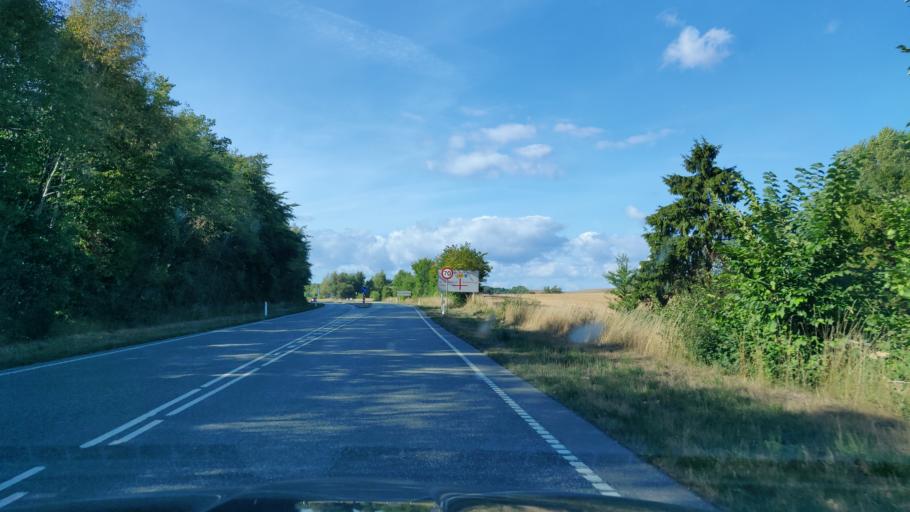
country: DK
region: Zealand
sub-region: Odsherred Kommune
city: Hojby
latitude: 55.9196
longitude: 11.5458
